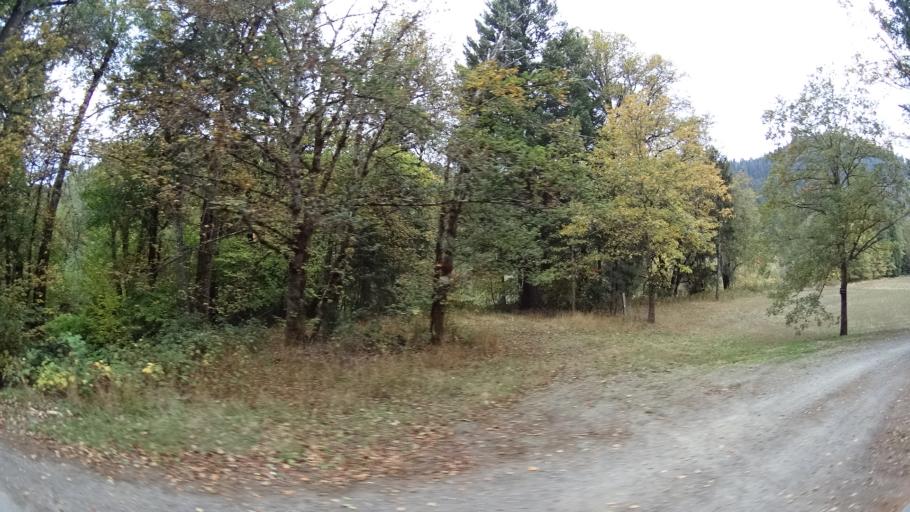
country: US
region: California
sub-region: Siskiyou County
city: Happy Camp
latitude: 41.7780
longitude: -123.3277
